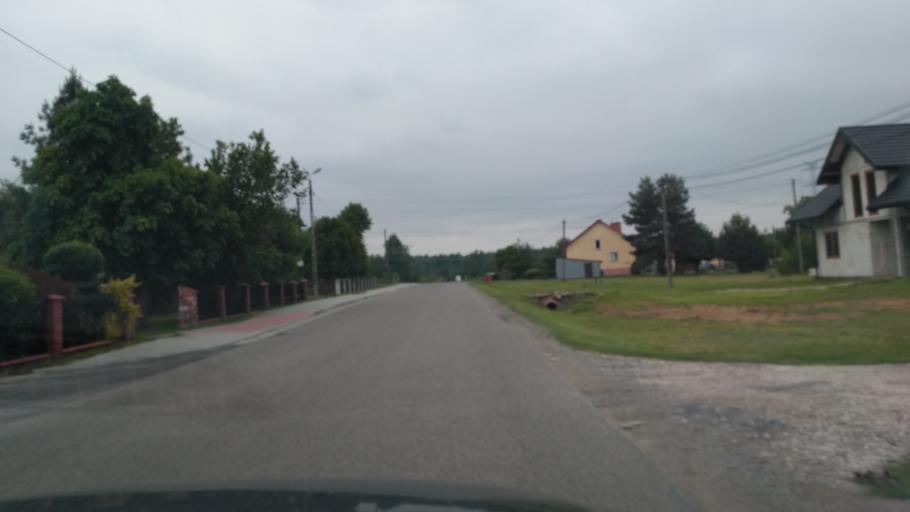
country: PL
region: Subcarpathian Voivodeship
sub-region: Powiat ropczycko-sedziszowski
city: Sedziszow Malopolski
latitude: 50.1411
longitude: 21.6699
